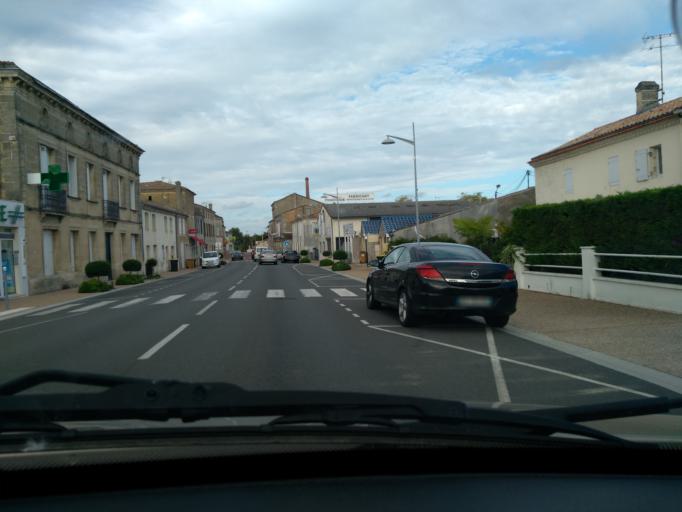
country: FR
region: Aquitaine
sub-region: Departement de la Gironde
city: Saint-Martin-Lacaussade
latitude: 45.1592
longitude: -0.6244
